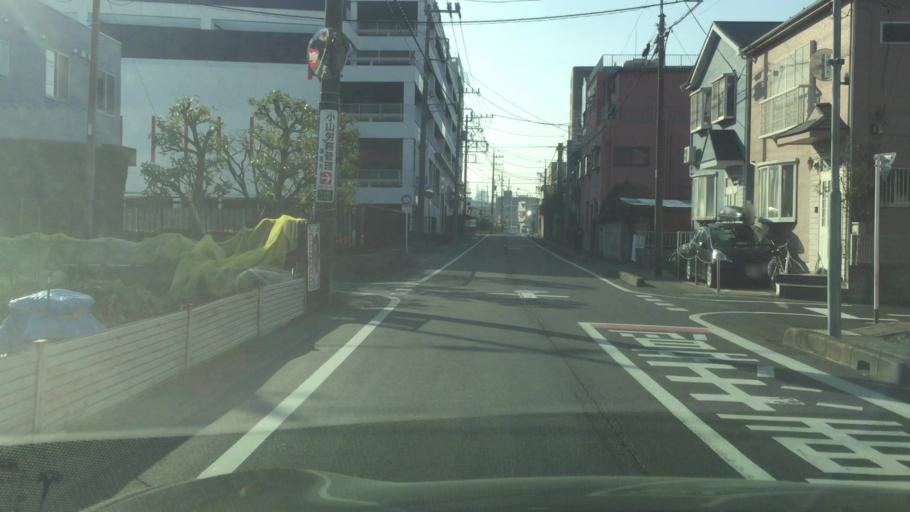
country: JP
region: Saitama
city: Ageoshimo
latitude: 35.9279
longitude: 139.6145
